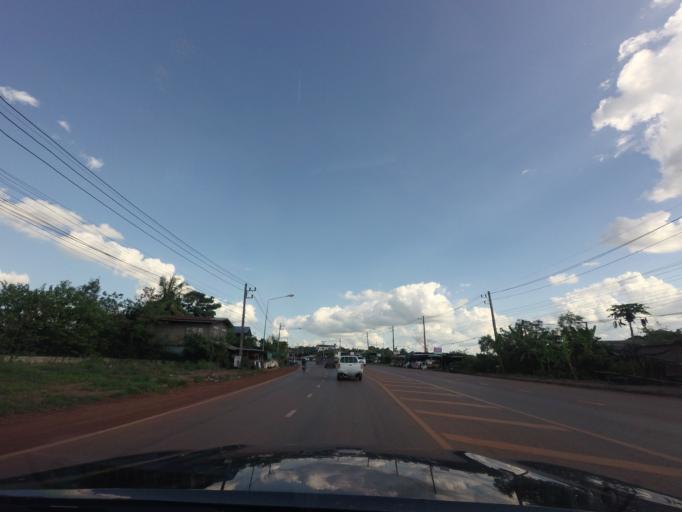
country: TH
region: Changwat Udon Thani
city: Ban Dung
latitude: 17.7057
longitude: 103.2518
